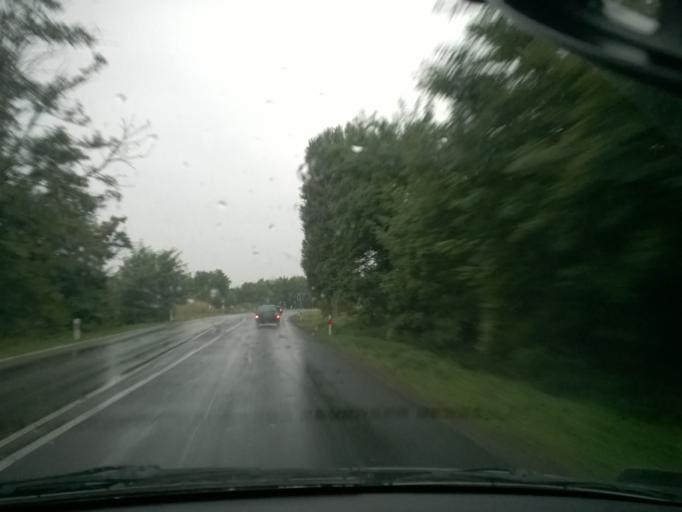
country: HU
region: Pest
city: Kiskunlachaza
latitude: 47.1578
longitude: 18.9985
